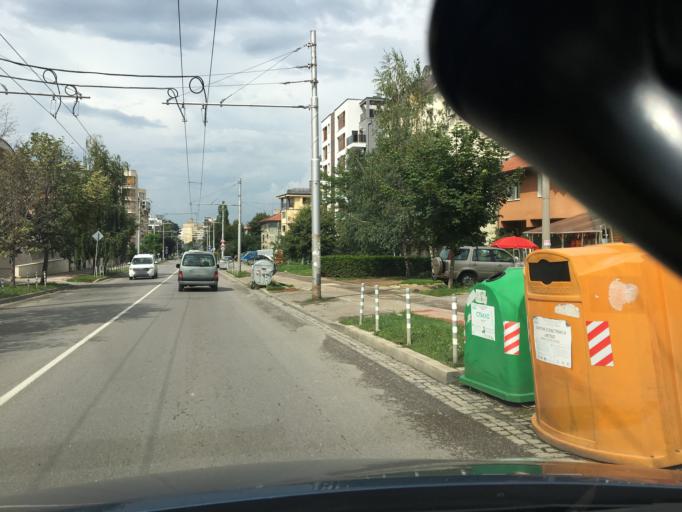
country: BG
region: Sofia-Capital
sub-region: Stolichna Obshtina
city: Sofia
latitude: 42.6618
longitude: 23.2737
